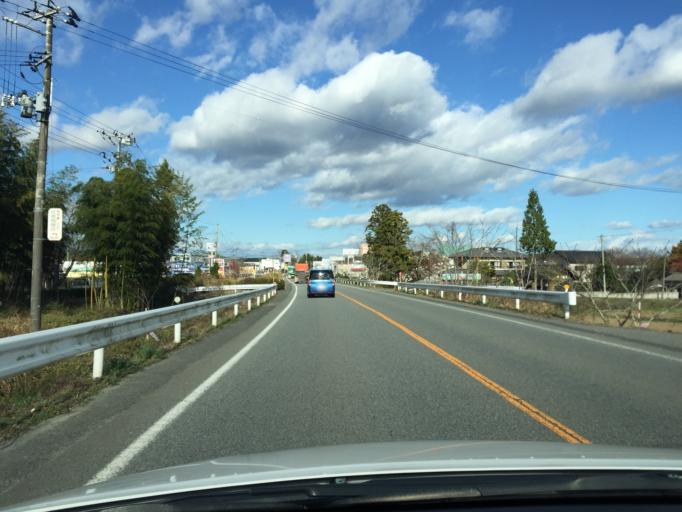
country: JP
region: Fukushima
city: Namie
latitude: 37.4813
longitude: 141.0068
